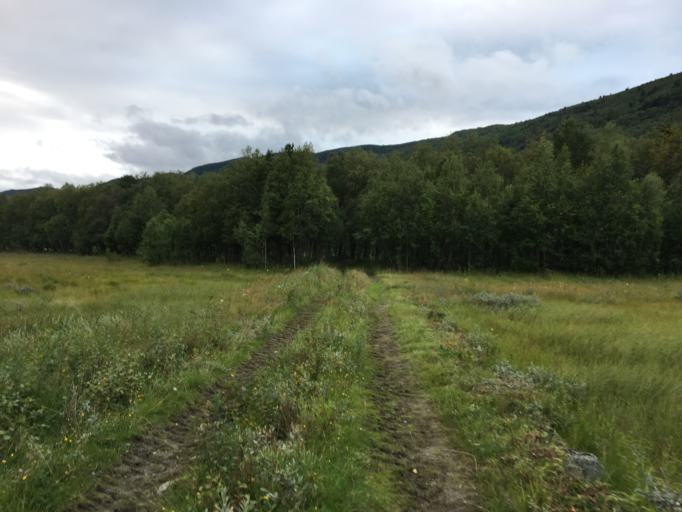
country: NO
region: Buskerud
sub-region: Hol
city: Hol
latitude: 60.6156
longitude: 8.2273
